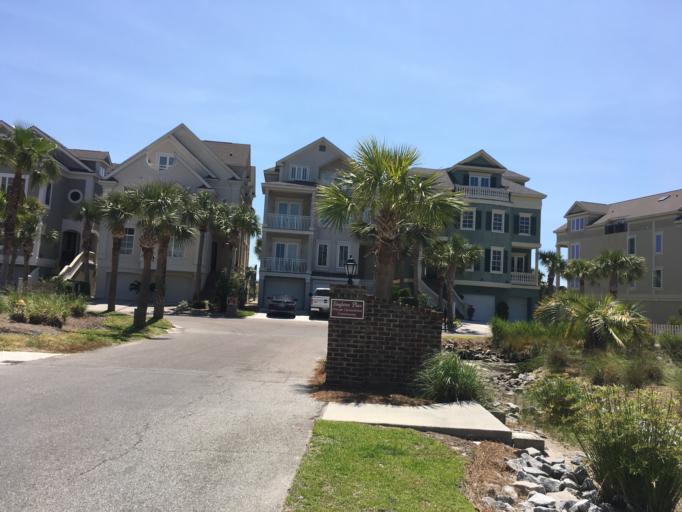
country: US
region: South Carolina
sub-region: Beaufort County
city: Hilton Head Island
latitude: 32.1891
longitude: -80.7011
